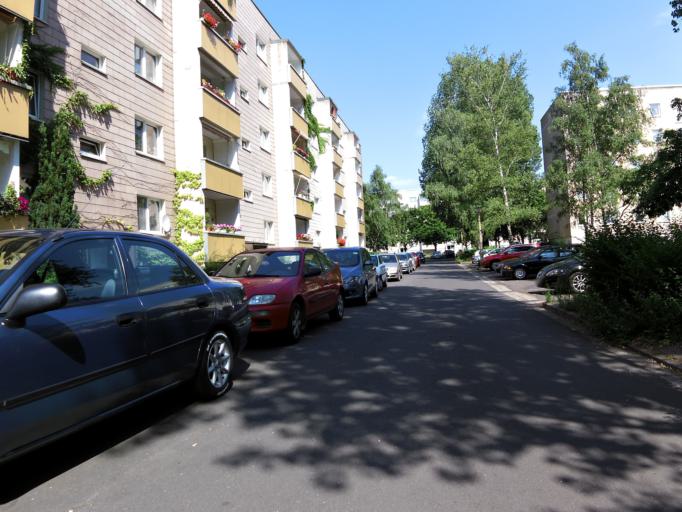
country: DE
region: Saxony
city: Leipzig
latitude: 51.3567
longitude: 12.4206
